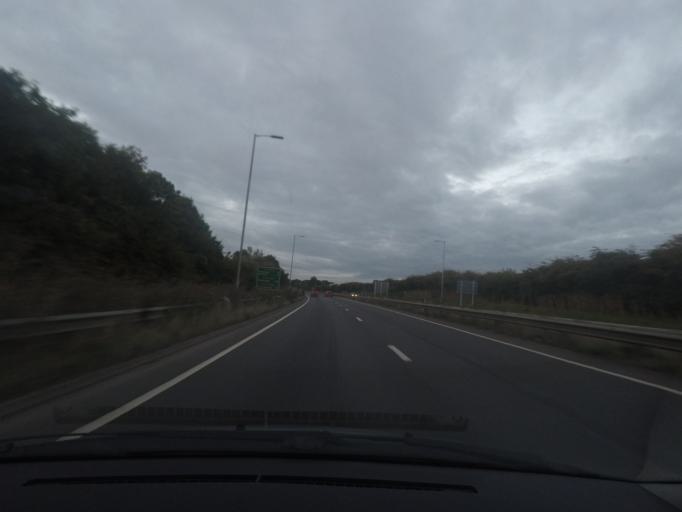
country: GB
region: England
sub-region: Northamptonshire
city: Rushden
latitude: 52.3019
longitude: -0.6153
